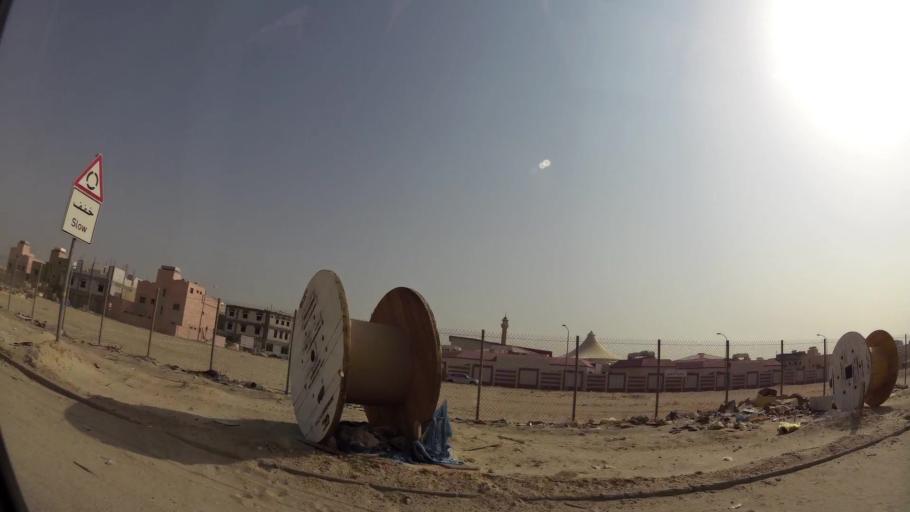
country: KW
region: Muhafazat al Jahra'
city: Al Jahra'
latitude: 29.3568
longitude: 47.7498
